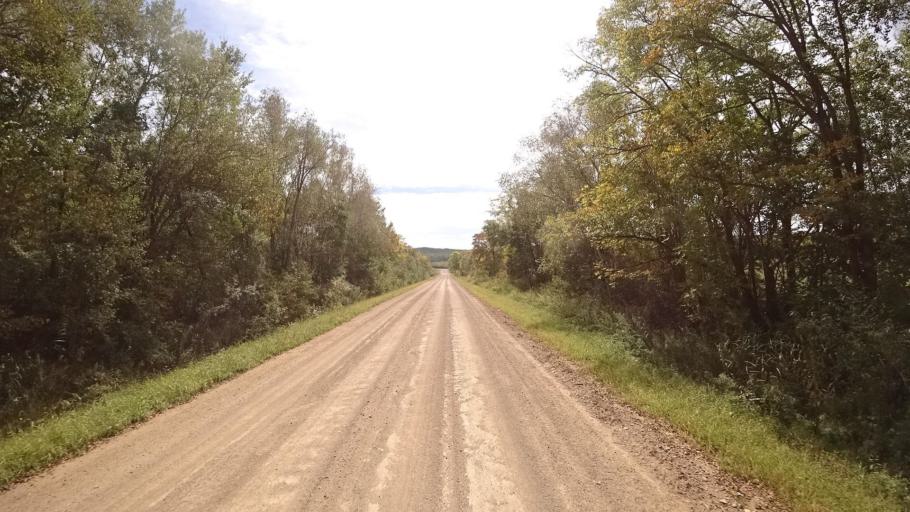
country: RU
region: Primorskiy
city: Yakovlevka
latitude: 44.6228
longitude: 133.5987
